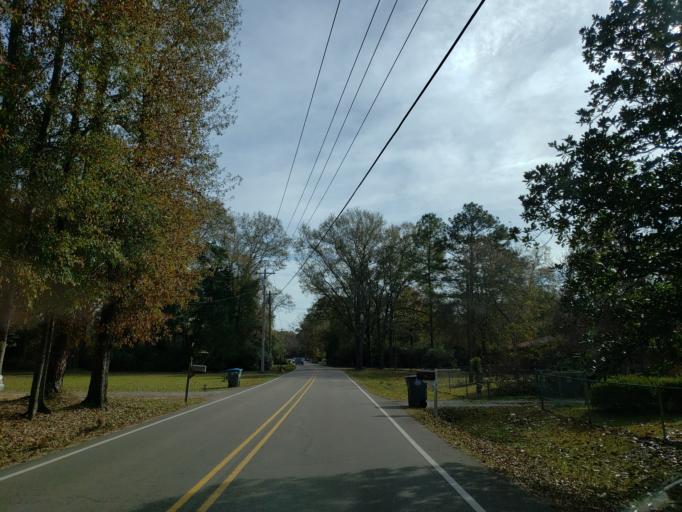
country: US
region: Mississippi
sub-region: Forrest County
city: Rawls Springs
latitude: 31.3832
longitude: -89.3722
